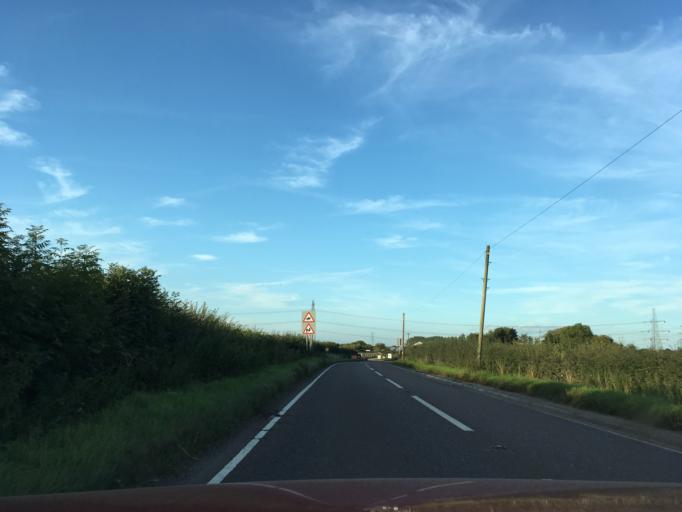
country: GB
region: England
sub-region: South Gloucestershire
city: Winterbourne
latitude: 51.5414
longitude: -2.4876
